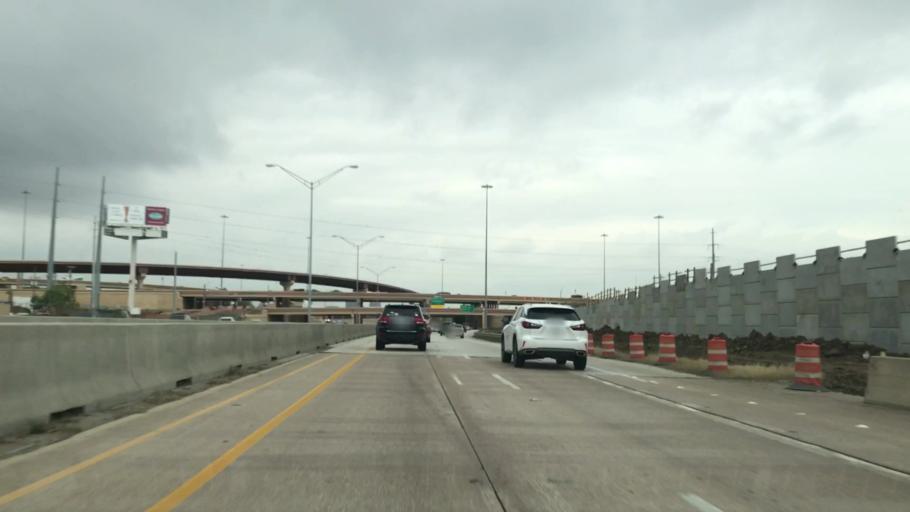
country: US
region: Texas
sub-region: Dallas County
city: Irving
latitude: 32.8430
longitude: -96.9090
